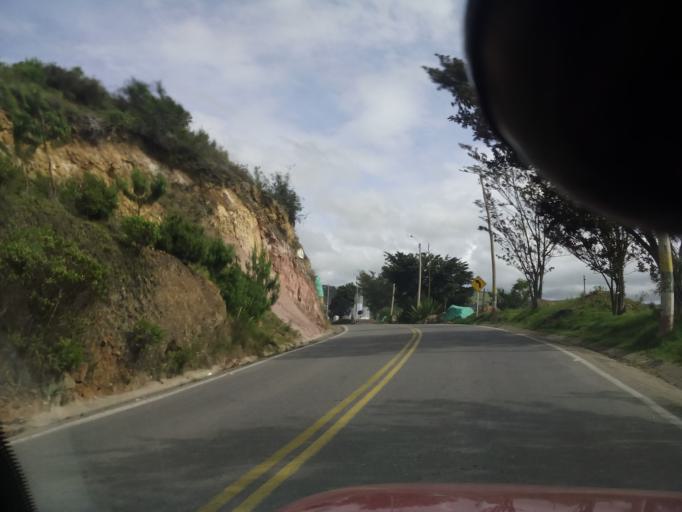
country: CO
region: Boyaca
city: Combita
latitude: 5.6312
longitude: -73.3177
